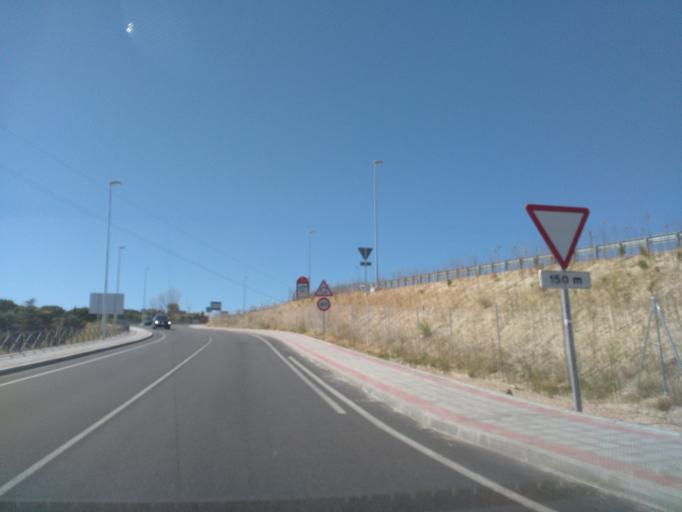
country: ES
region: Madrid
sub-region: Provincia de Madrid
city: Villanueva del Pardillo
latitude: 40.4845
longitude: -3.9388
